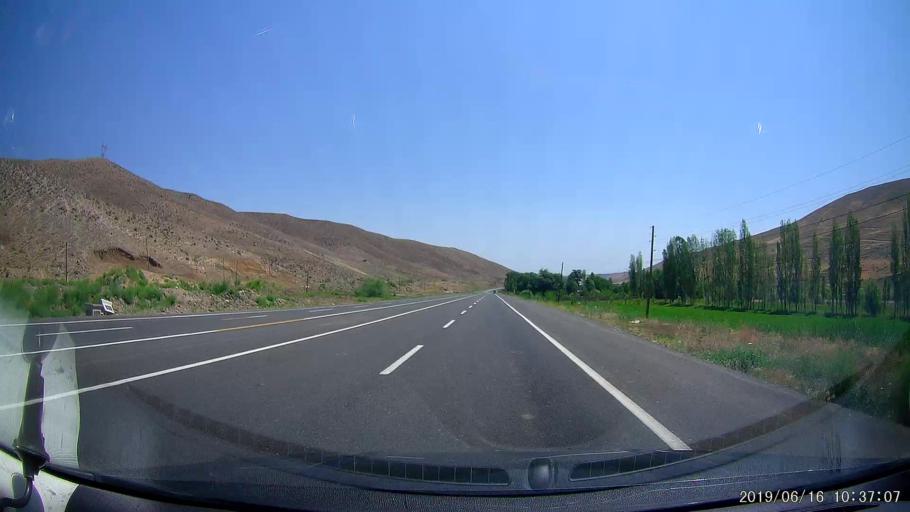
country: TR
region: Igdir
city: Tuzluca
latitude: 40.0443
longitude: 43.6930
